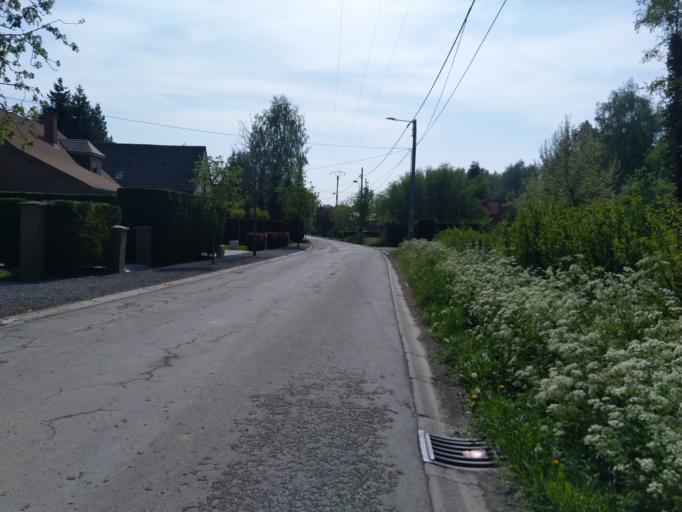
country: BE
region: Wallonia
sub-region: Province du Hainaut
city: Mons
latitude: 50.4440
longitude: 4.0231
